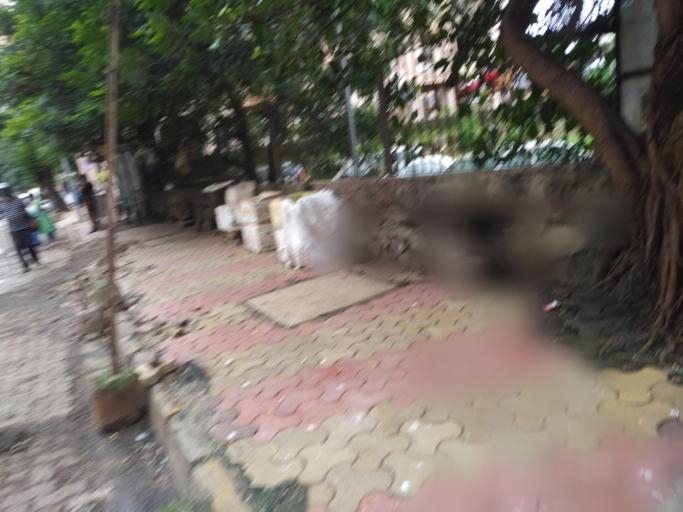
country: IN
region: Maharashtra
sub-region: Mumbai Suburban
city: Borivli
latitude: 19.2368
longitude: 72.8641
